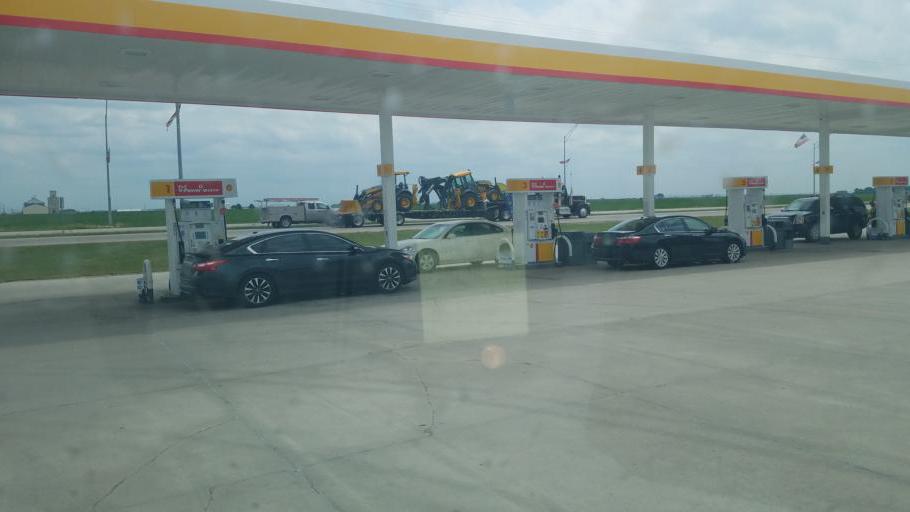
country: US
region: Nebraska
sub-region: York County
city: York
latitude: 40.8139
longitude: -97.5984
